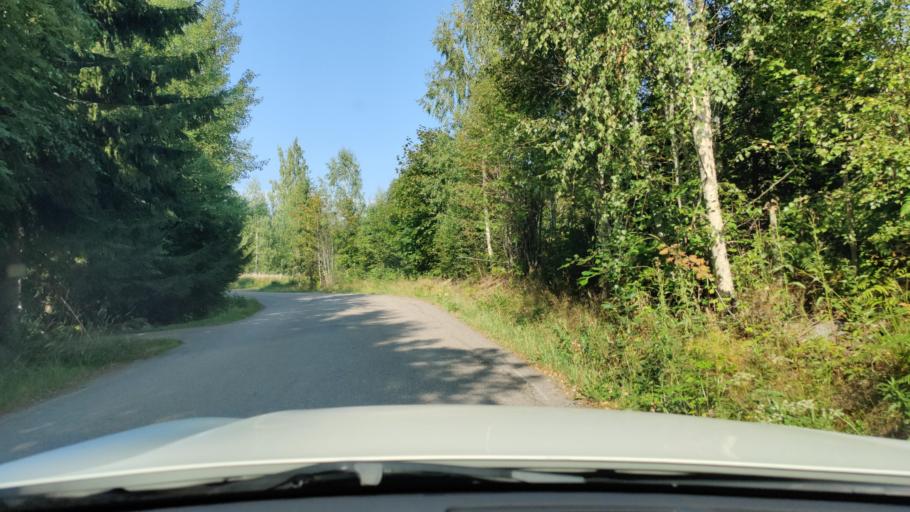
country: FI
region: Haeme
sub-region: Haemeenlinna
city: Tervakoski
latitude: 60.6768
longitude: 24.6250
